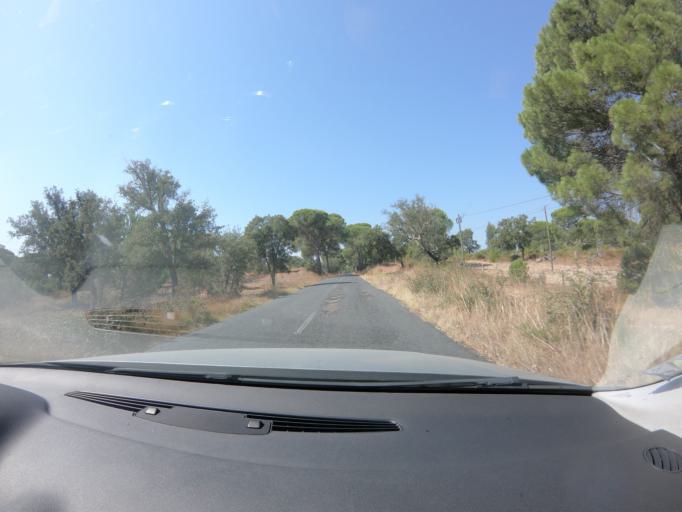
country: PT
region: Setubal
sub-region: Alcacer do Sal
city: Alcacer do Sal
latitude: 38.2662
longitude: -8.3210
